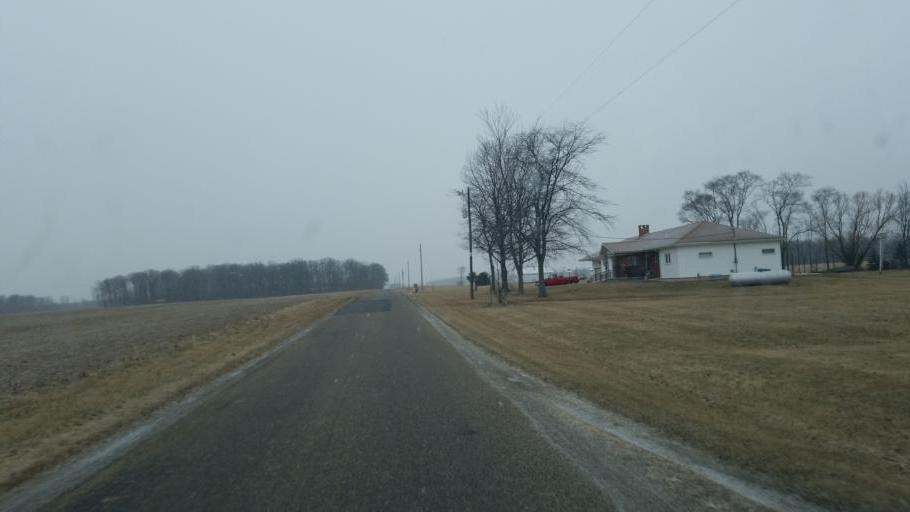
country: US
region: Ohio
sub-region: Defiance County
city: Hicksville
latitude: 41.3393
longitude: -84.7321
